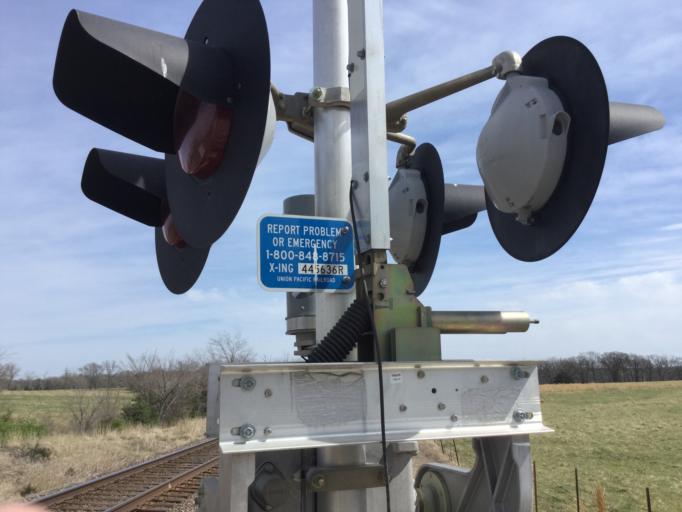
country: US
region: Kansas
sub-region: Montgomery County
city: Independence
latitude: 37.2692
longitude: -95.7409
